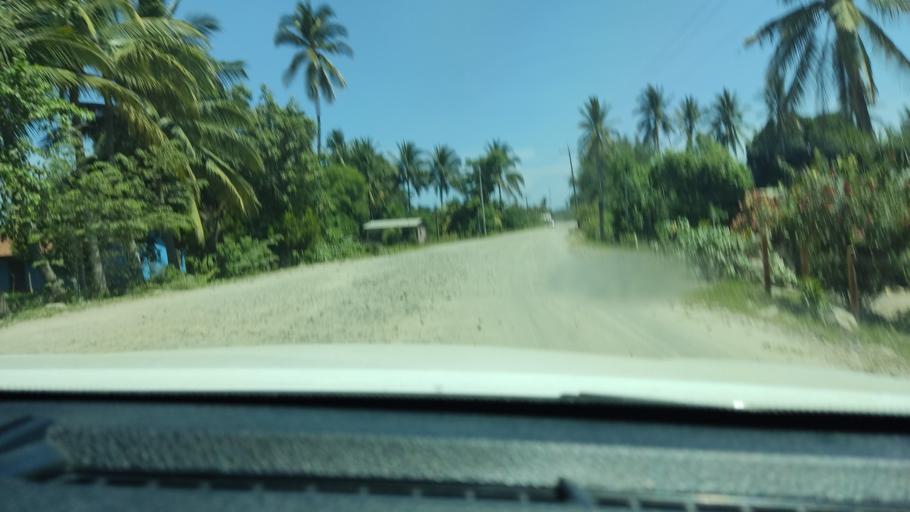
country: SV
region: Ahuachapan
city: San Francisco Menendez
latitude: 13.7637
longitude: -90.1161
